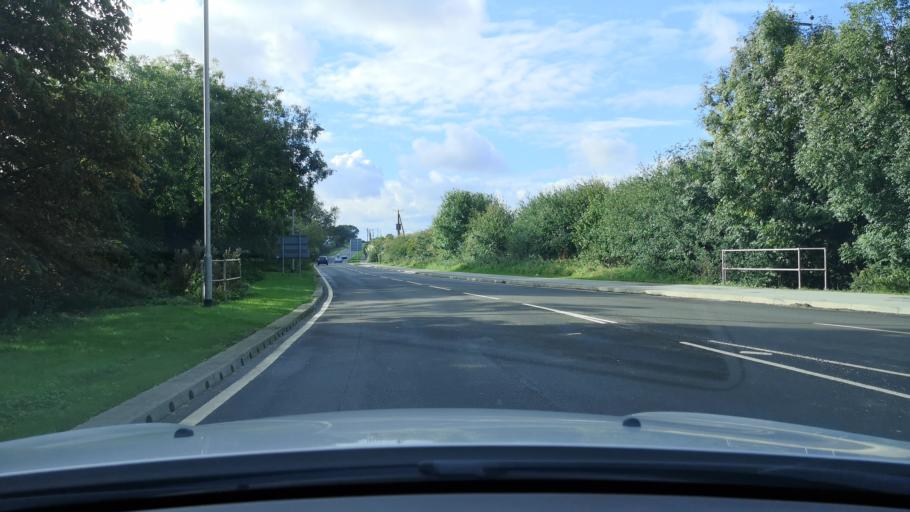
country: GB
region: England
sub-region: East Riding of Yorkshire
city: Leconfield
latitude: 53.8542
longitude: -0.4558
